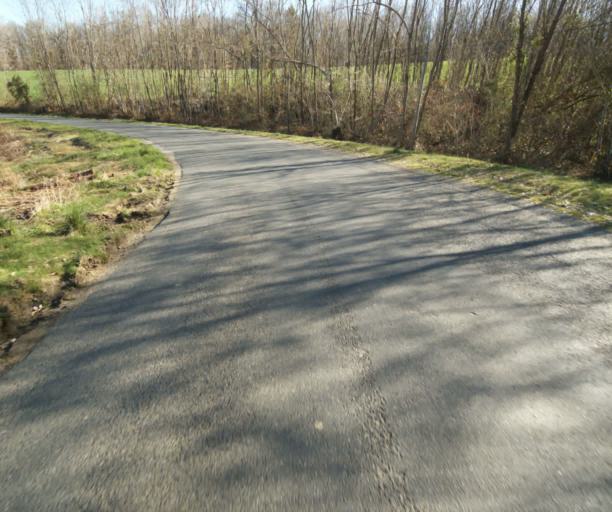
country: FR
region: Limousin
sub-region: Departement de la Correze
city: Seilhac
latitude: 45.3969
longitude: 1.7474
